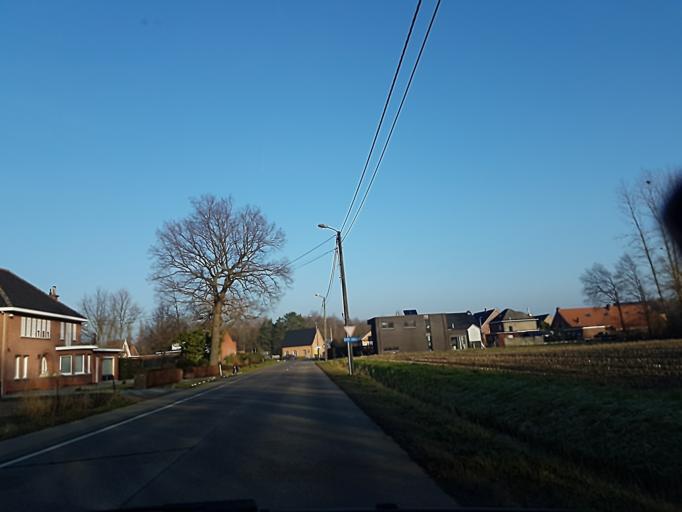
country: BE
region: Flanders
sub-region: Provincie Antwerpen
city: Heist-op-den-Berg
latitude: 51.0421
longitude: 4.7214
